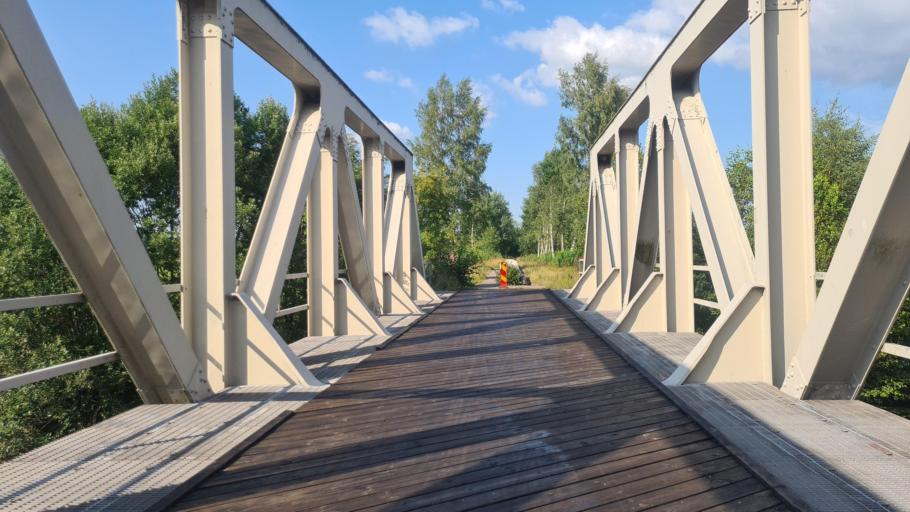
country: SE
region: Kronoberg
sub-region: Ljungby Kommun
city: Ljungby
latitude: 56.7931
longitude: 13.9074
